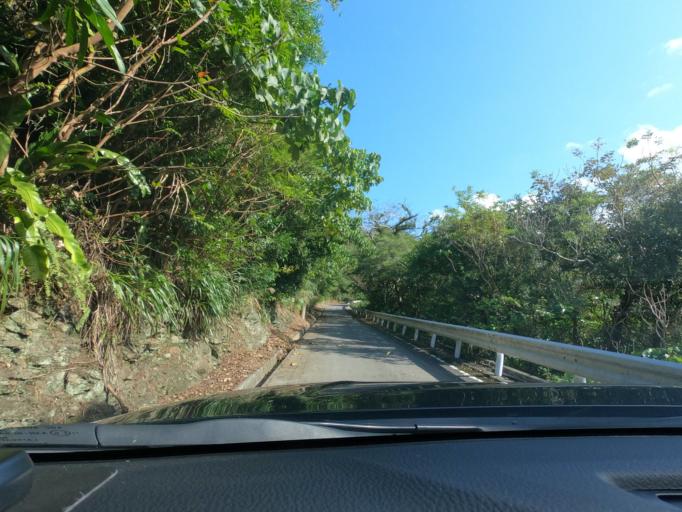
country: JP
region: Okinawa
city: Nago
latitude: 26.7568
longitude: 128.1948
